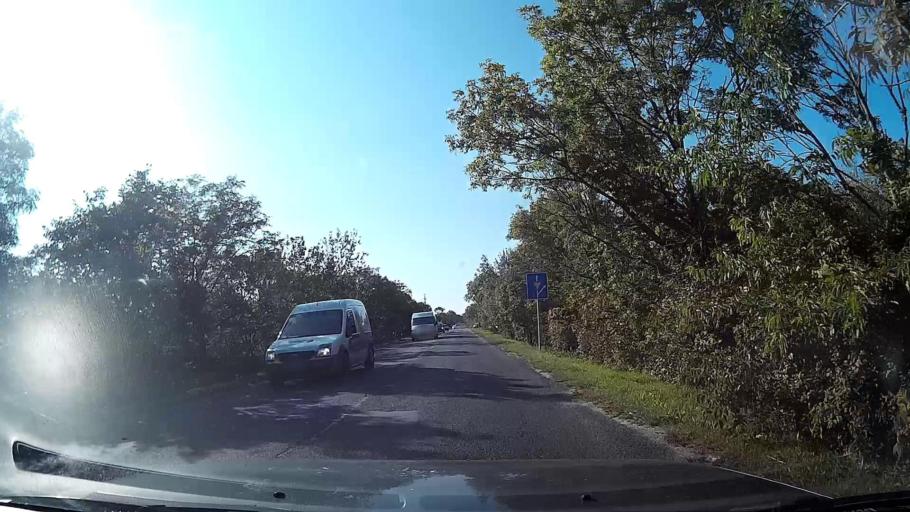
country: HU
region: Pest
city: Diosd
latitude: 47.4217
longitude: 18.9778
